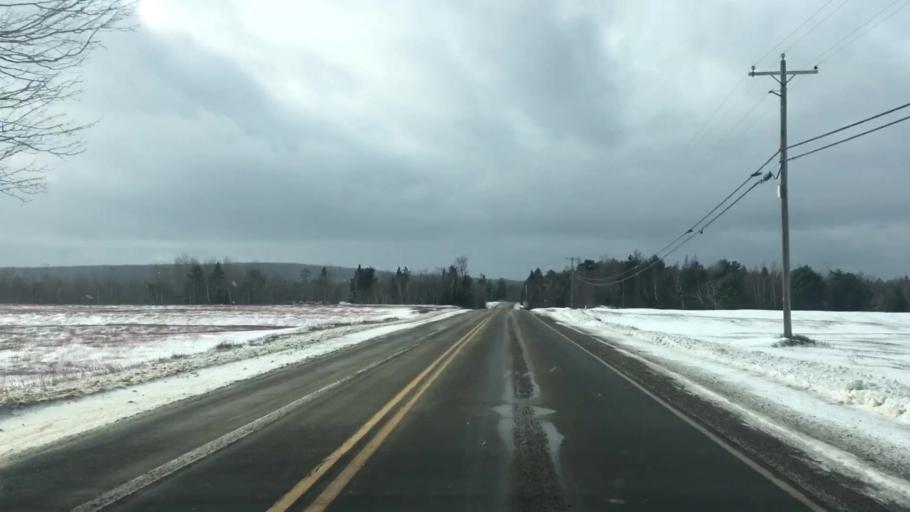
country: US
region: Maine
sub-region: Washington County
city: Calais
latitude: 45.0217
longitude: -67.3794
